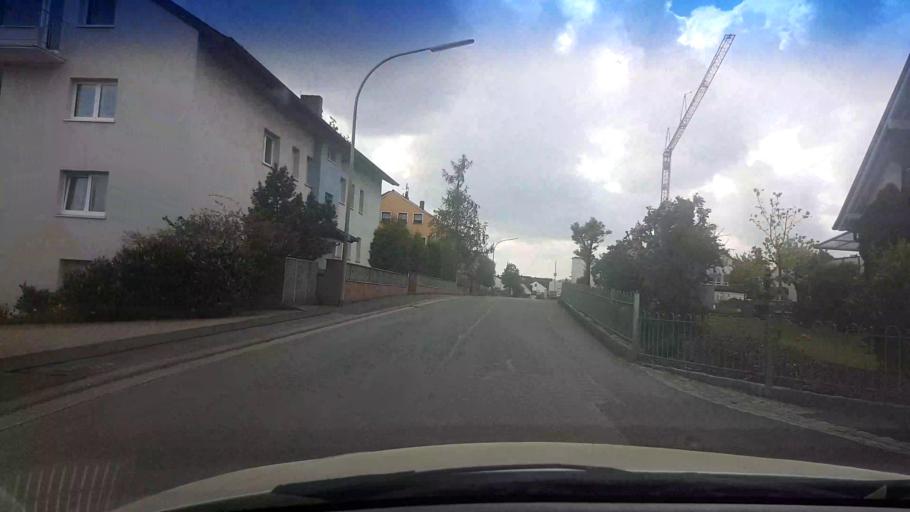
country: DE
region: Bavaria
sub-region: Upper Franconia
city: Pettstadt
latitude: 49.8335
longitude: 10.9344
